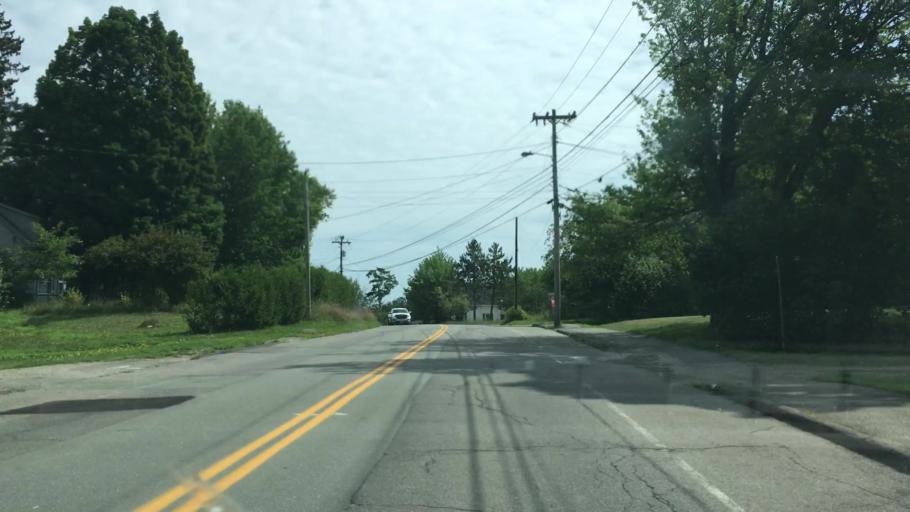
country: US
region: Maine
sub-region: Washington County
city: Calais
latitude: 45.1710
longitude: -67.2832
